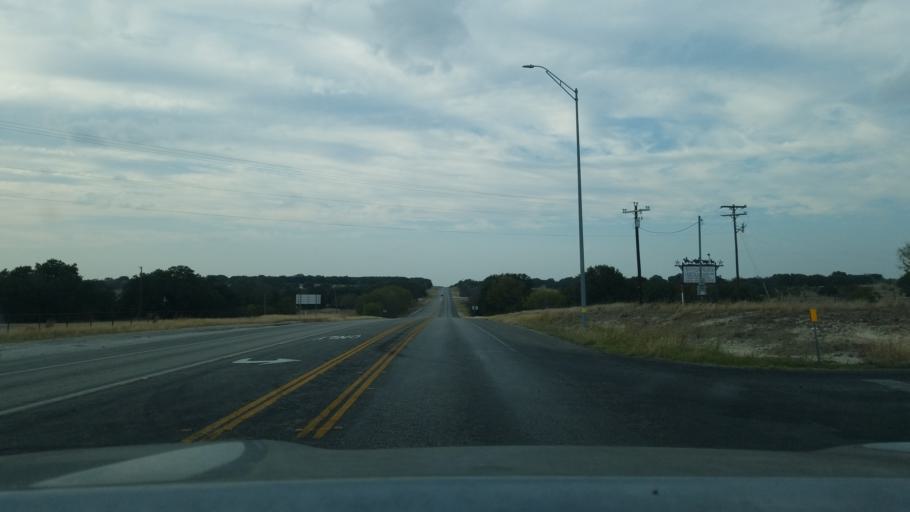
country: US
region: Texas
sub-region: Mills County
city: Goldthwaite
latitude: 31.5207
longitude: -98.5961
